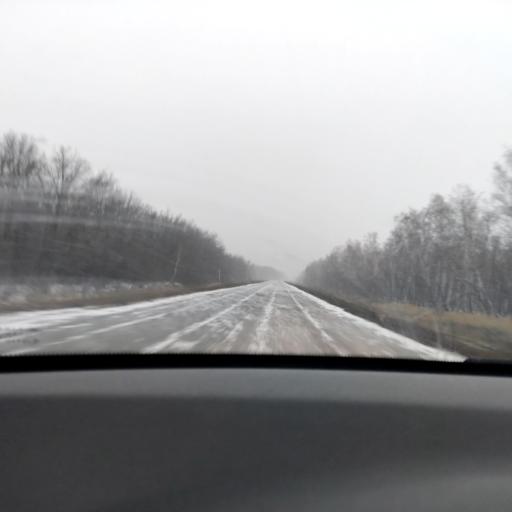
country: RU
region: Samara
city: Novokuybyshevsk
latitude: 52.9512
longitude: 49.8938
